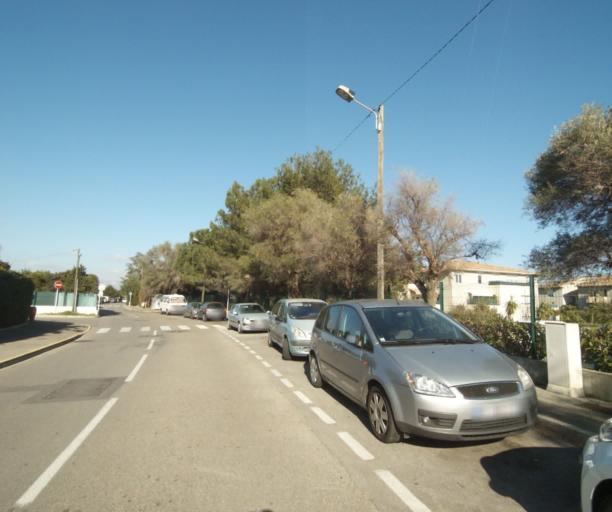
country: FR
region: Provence-Alpes-Cote d'Azur
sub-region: Departement des Alpes-Maritimes
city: Biot
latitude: 43.6061
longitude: 7.1178
